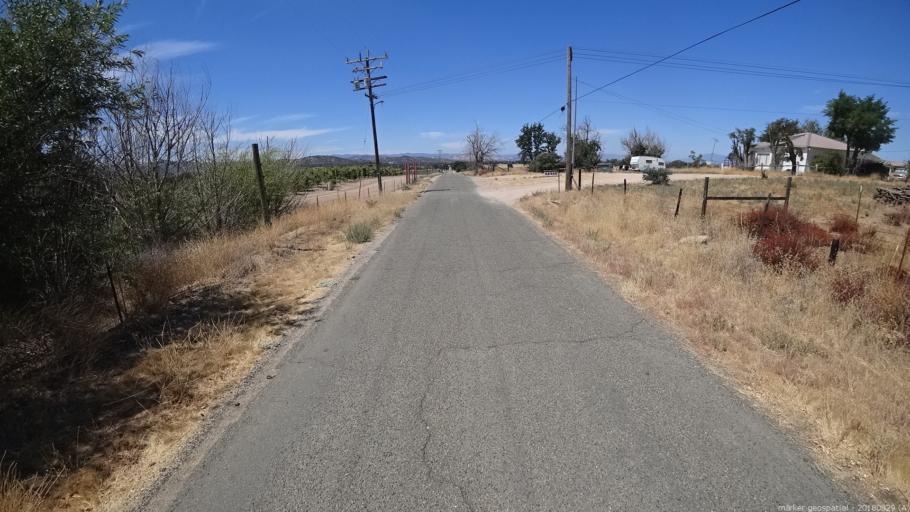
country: US
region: California
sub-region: San Luis Obispo County
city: Lake Nacimiento
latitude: 35.9224
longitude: -121.0452
